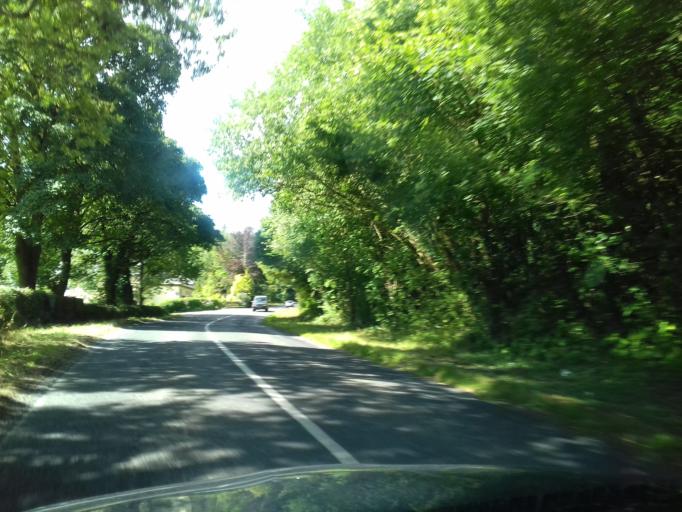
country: IE
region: Munster
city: Carrick-on-Suir
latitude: 52.4033
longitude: -7.4825
